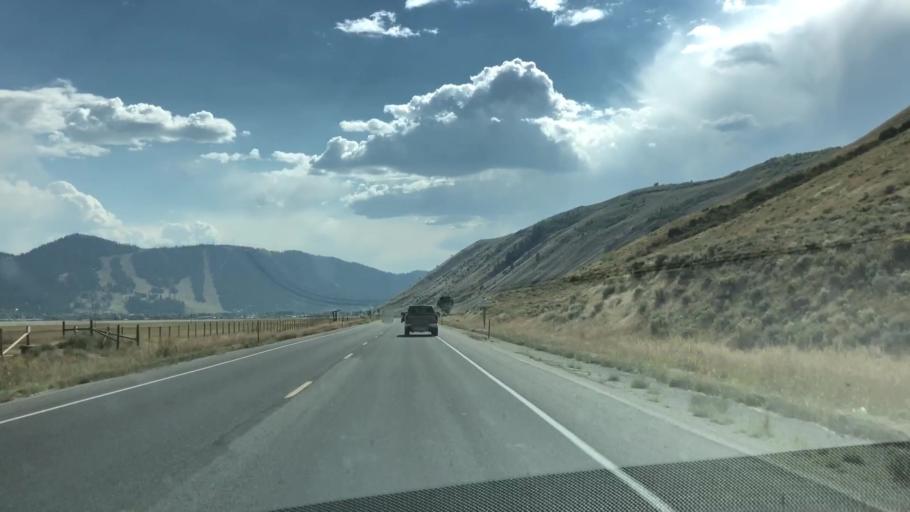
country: US
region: Wyoming
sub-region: Teton County
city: Jackson
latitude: 43.5141
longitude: -110.7507
